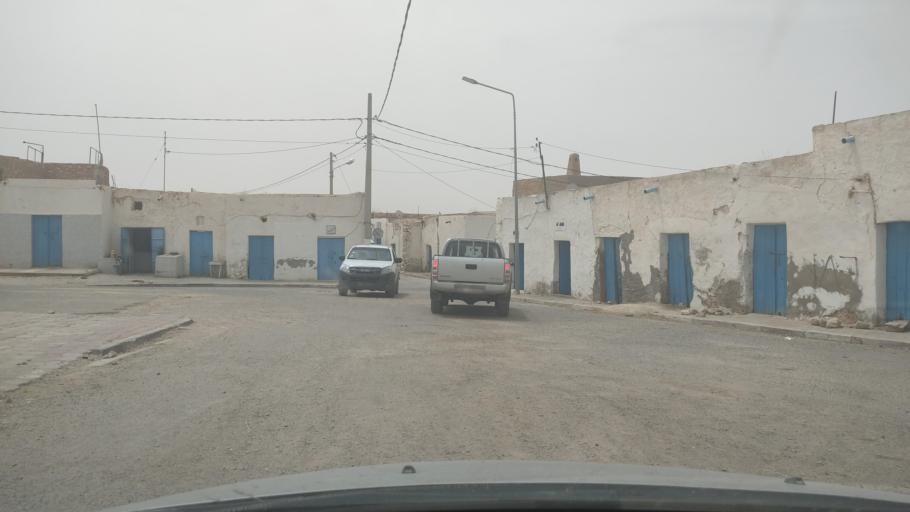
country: TN
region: Gafsa
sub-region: Gafsa Municipality
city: Gafsa
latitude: 34.3346
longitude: 8.9521
